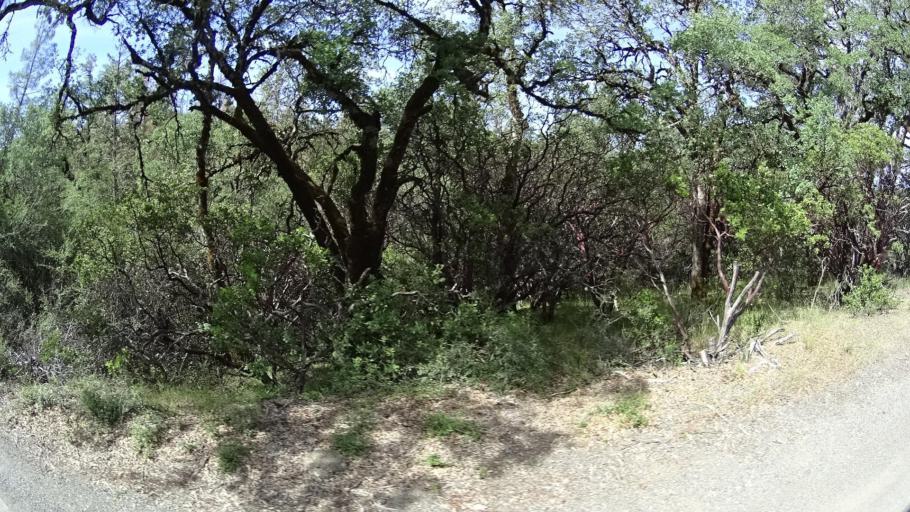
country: US
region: California
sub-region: Lake County
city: Cobb
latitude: 38.8638
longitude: -122.7433
